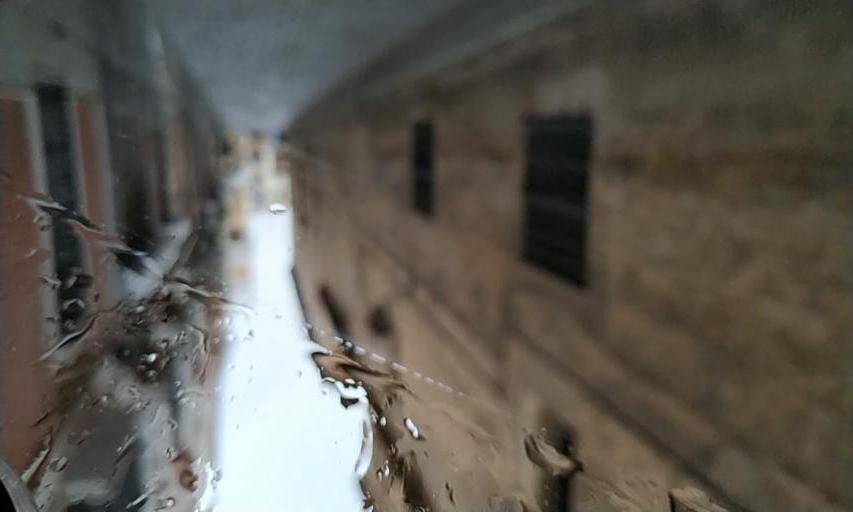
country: ES
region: Extremadura
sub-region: Provincia de Badajoz
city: Badajoz
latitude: 38.8785
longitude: -6.9689
